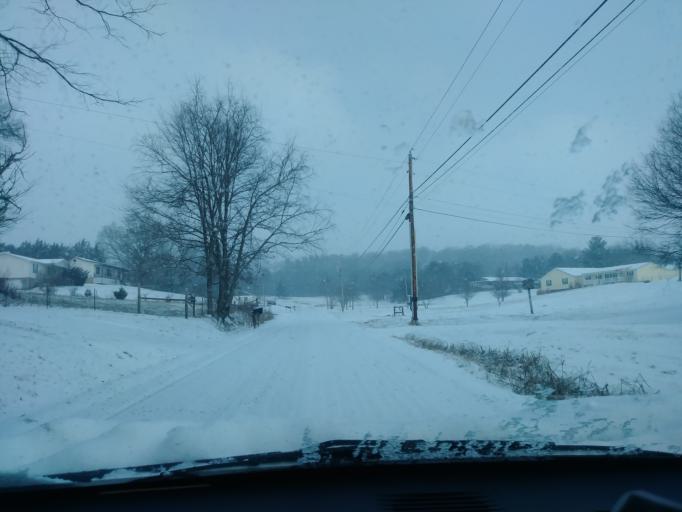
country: US
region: Tennessee
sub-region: Greene County
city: Mosheim
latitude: 36.1019
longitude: -82.9270
